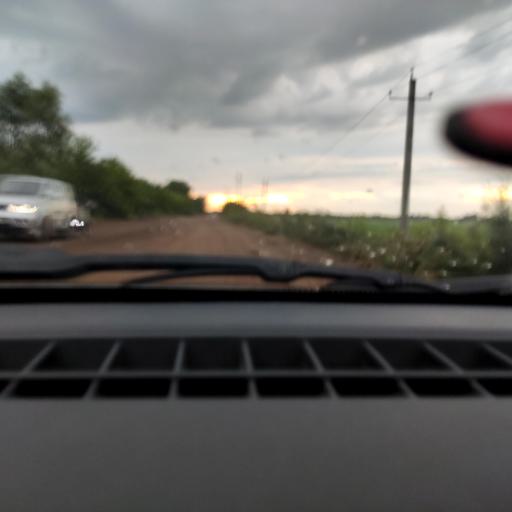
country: RU
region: Bashkortostan
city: Blagoveshchensk
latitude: 54.9173
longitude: 55.9832
